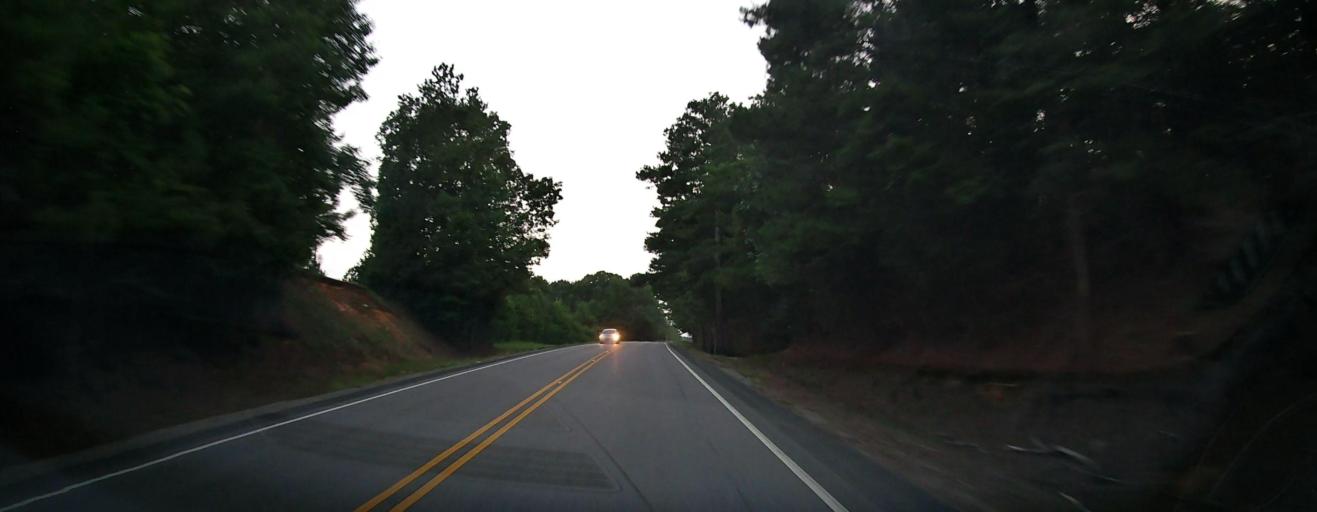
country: US
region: Alabama
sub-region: Marion County
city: Hamilton
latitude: 34.1258
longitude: -88.0340
